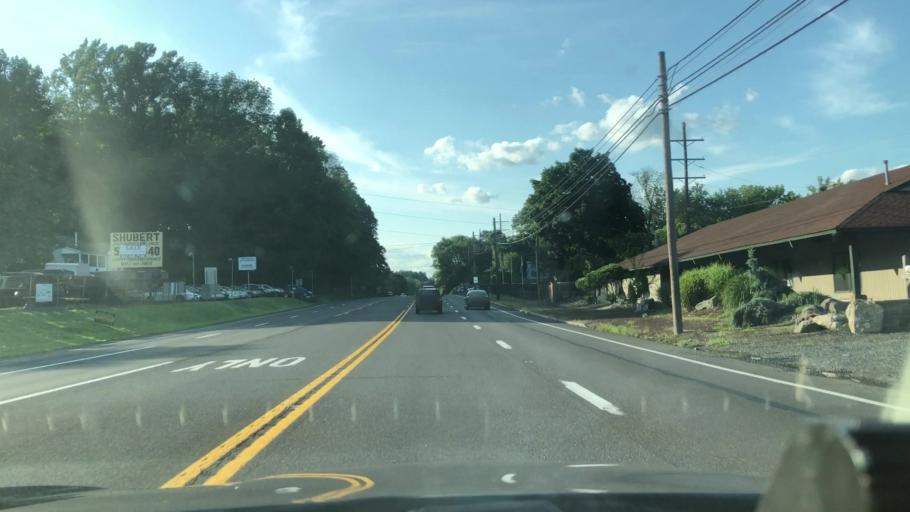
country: US
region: Pennsylvania
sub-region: Lehigh County
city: Coopersburg
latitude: 40.4812
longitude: -75.3750
